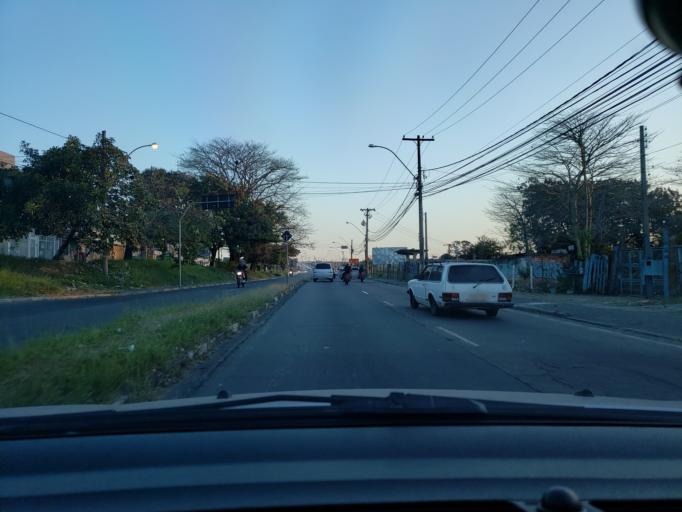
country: BR
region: Sao Paulo
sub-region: Campinas
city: Campinas
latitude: -22.9284
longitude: -47.1276
